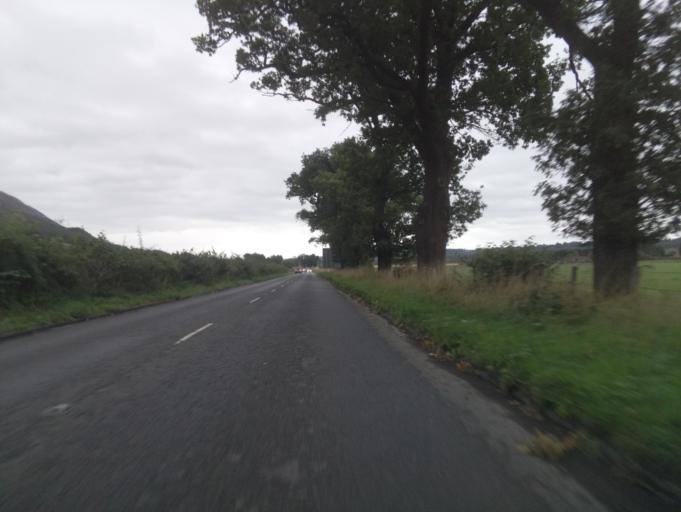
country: GB
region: Scotland
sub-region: Clackmannanshire
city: Alva
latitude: 56.1524
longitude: -3.7830
